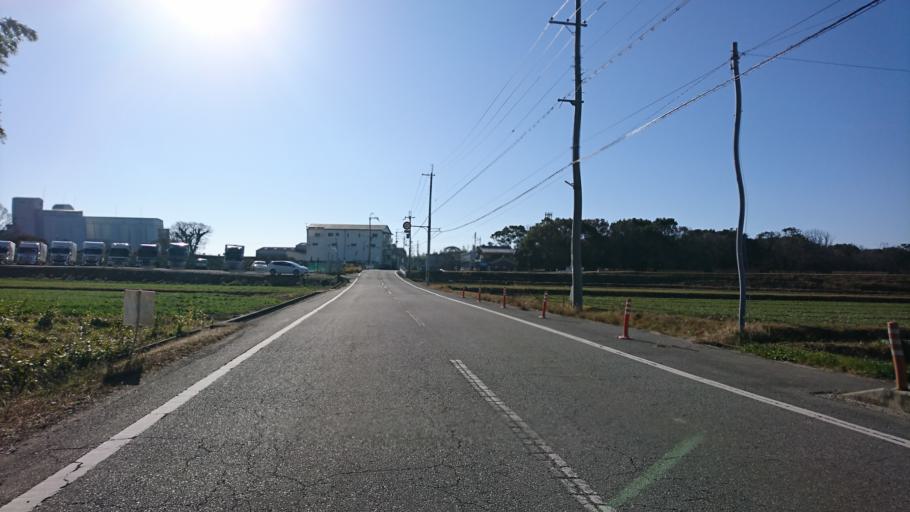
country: JP
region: Hyogo
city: Miki
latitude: 34.7567
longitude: 134.9255
